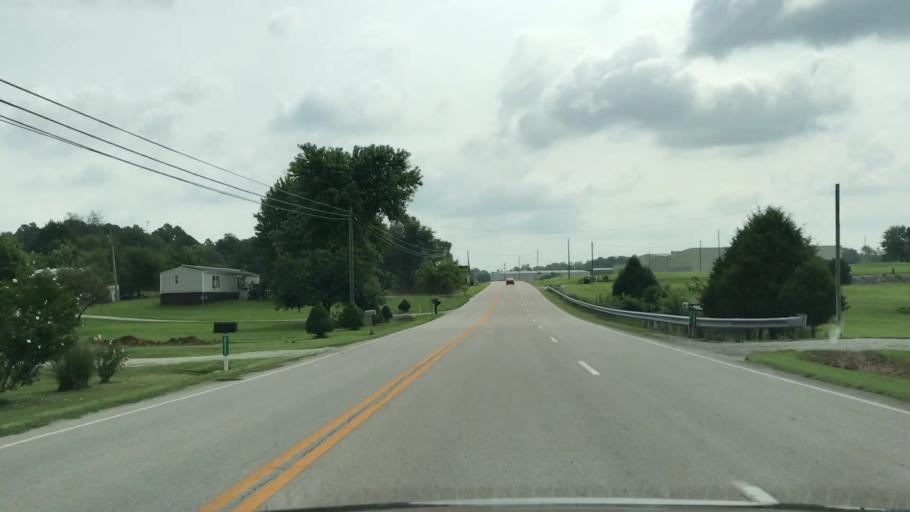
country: US
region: Kentucky
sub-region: Barren County
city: Cave City
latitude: 37.0906
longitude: -86.0782
